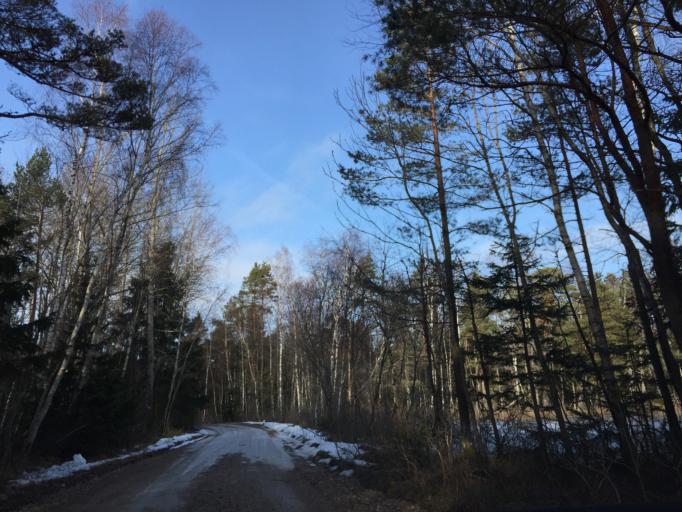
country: EE
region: Saare
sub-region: Kuressaare linn
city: Kuressaare
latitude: 58.4778
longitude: 21.9514
